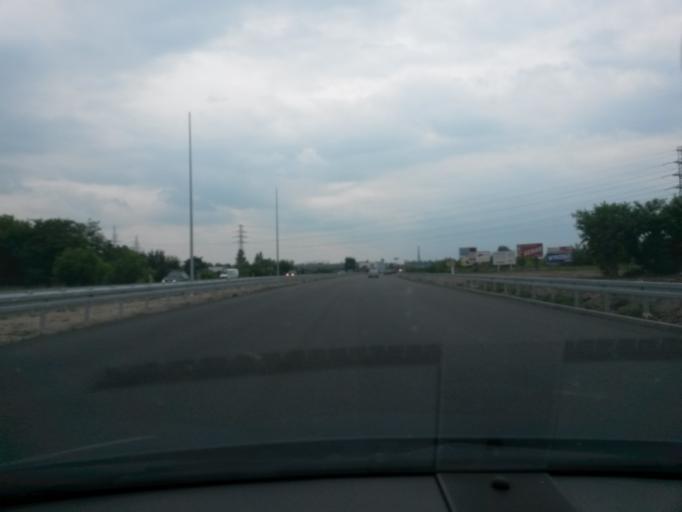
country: PL
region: Silesian Voivodeship
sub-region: Czestochowa
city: Czestochowa
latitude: 50.8298
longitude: 19.1450
